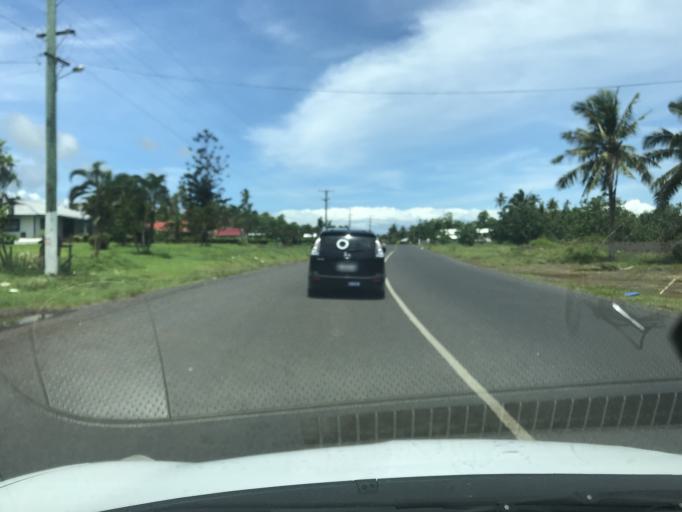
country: WS
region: Tuamasaga
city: Malie
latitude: -13.7988
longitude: -171.8398
